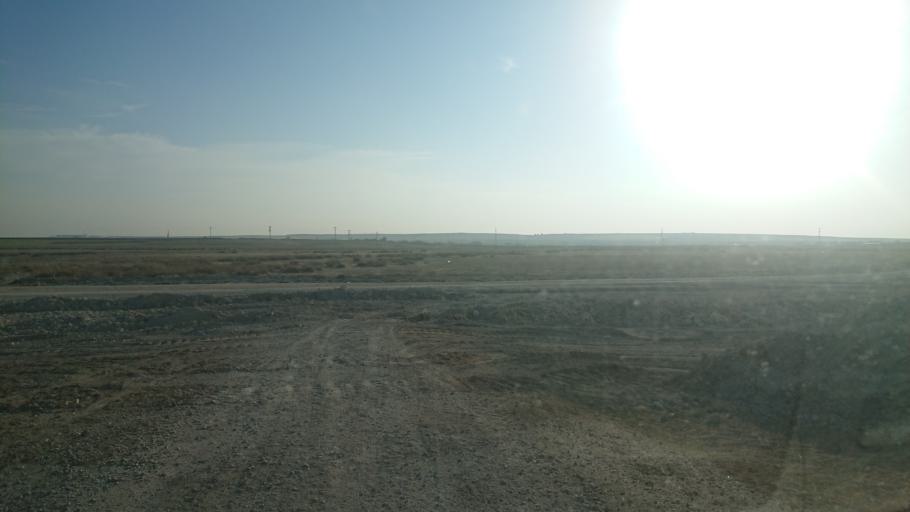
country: TR
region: Aksaray
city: Sultanhani
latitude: 38.1403
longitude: 33.5721
